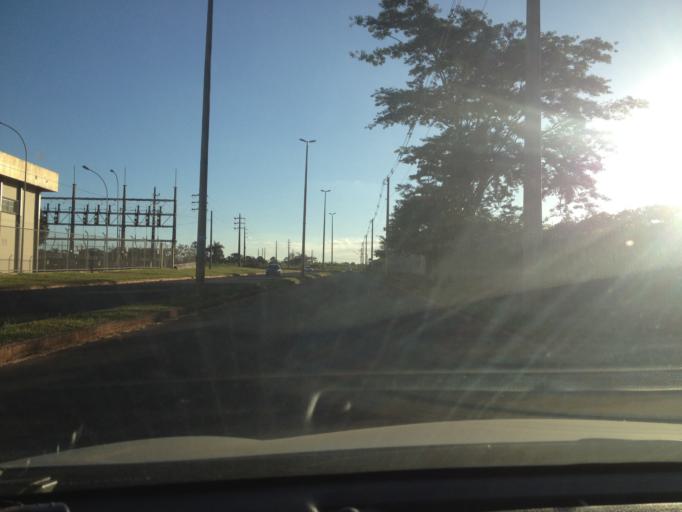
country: BR
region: Federal District
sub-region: Brasilia
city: Brasilia
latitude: -15.7580
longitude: -47.8979
